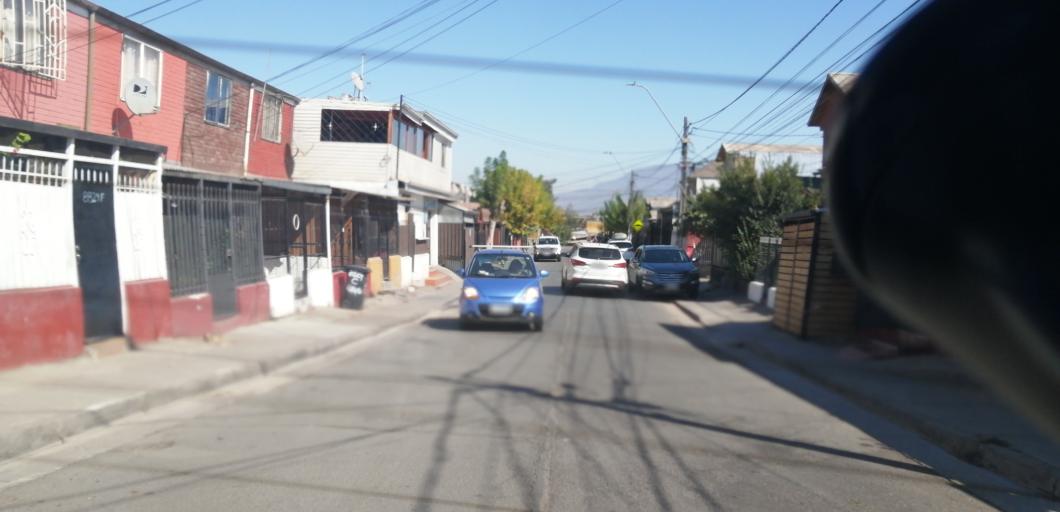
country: CL
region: Santiago Metropolitan
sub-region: Provincia de Santiago
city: Lo Prado
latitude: -33.4456
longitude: -70.7579
